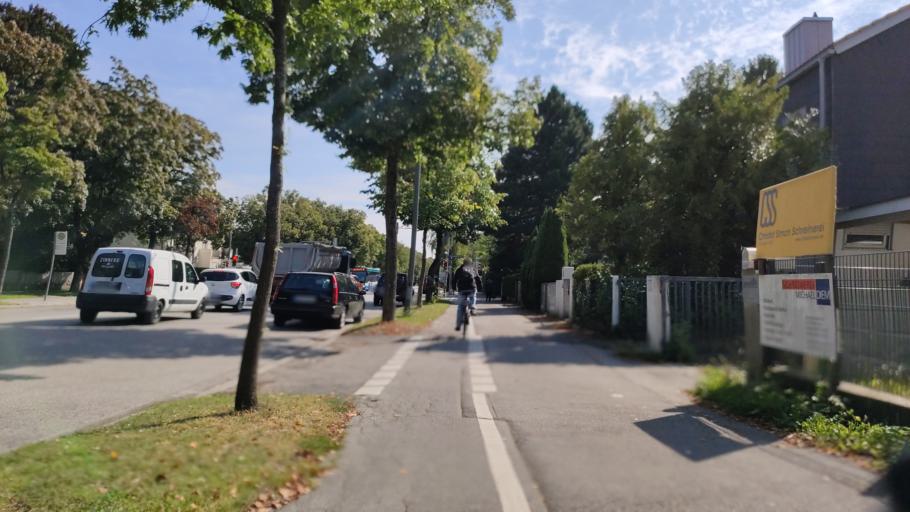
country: DE
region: Bavaria
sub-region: Upper Bavaria
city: Neuried
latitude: 48.1138
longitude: 11.4867
